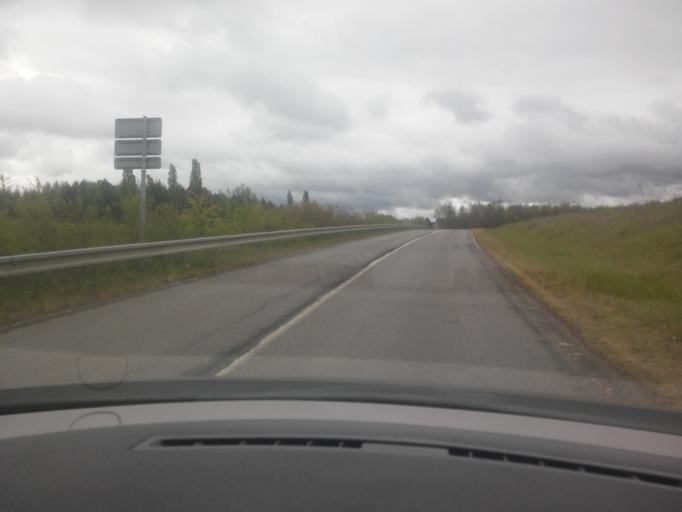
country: FR
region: Lorraine
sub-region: Departement de la Moselle
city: Mecleuves
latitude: 49.0493
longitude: 6.2573
